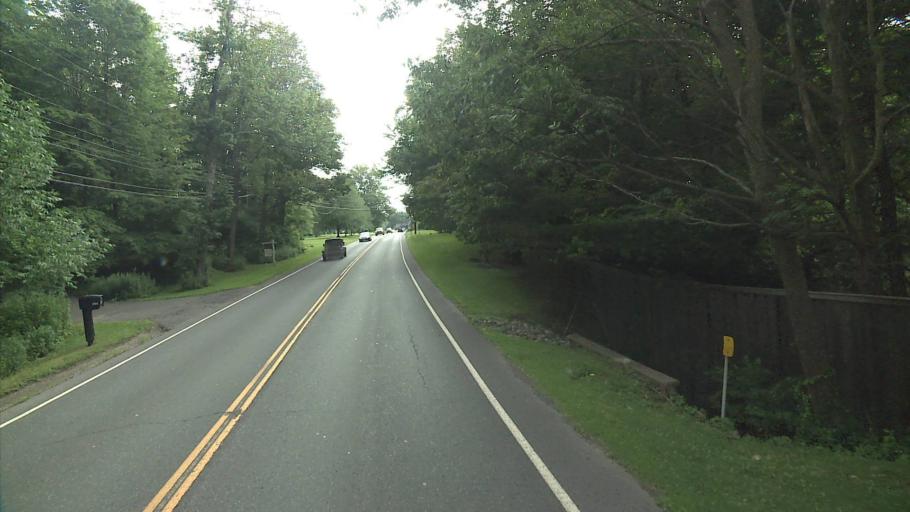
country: US
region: Connecticut
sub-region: New Haven County
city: Southbury
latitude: 41.4937
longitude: -73.2130
